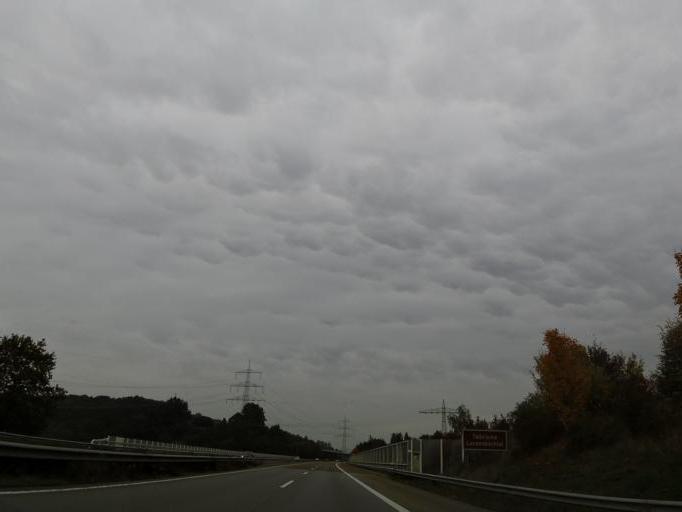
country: DE
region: Rheinland-Pfalz
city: Sembach
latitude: 49.5228
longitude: 7.8459
